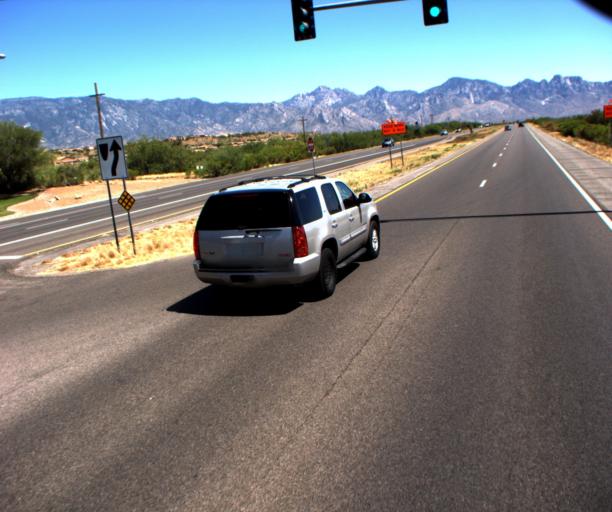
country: US
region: Arizona
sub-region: Pima County
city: Catalina
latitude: 32.5240
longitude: -110.9283
